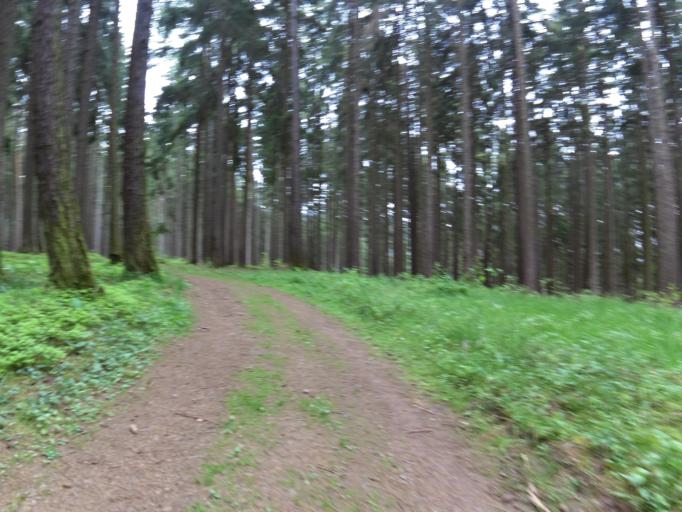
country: DE
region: Thuringia
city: Georgenthal
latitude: 50.8232
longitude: 10.6630
